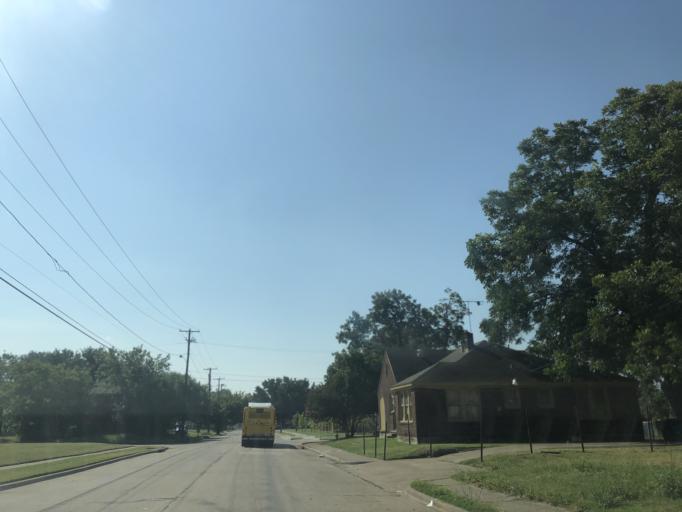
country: US
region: Texas
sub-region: Dallas County
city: Dallas
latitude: 32.7647
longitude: -96.7725
